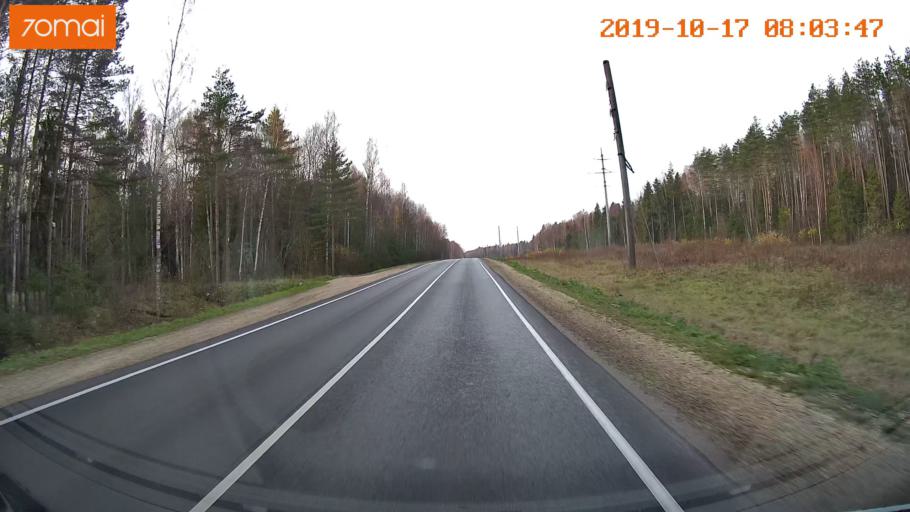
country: RU
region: Vladimir
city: Belaya Rechka
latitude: 56.3522
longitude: 39.4484
